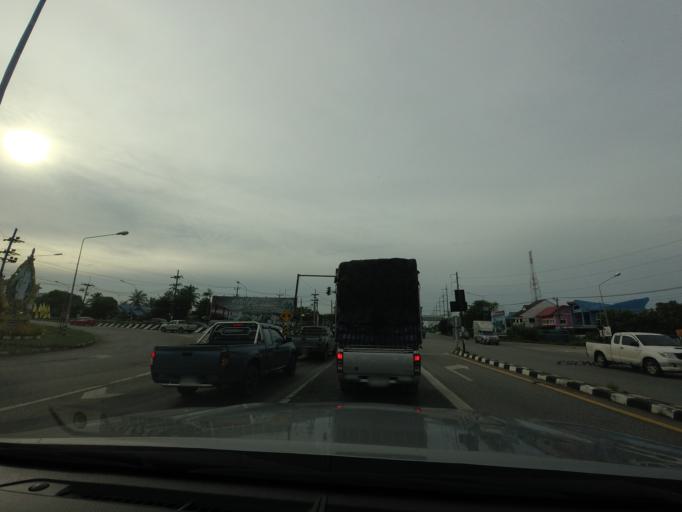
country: TH
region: Songkhla
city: Ranot
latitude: 7.7841
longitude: 100.3530
